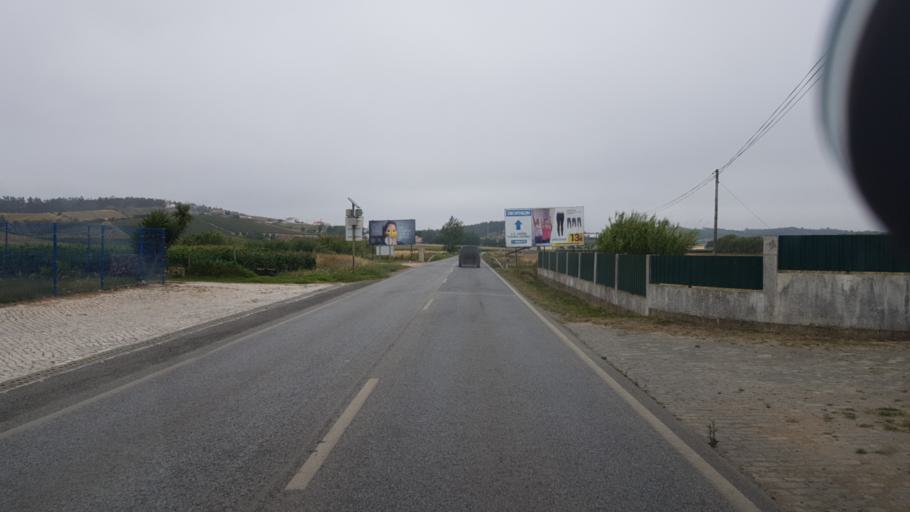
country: PT
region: Lisbon
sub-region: Torres Vedras
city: Torres Vedras
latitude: 39.0923
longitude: -9.2999
